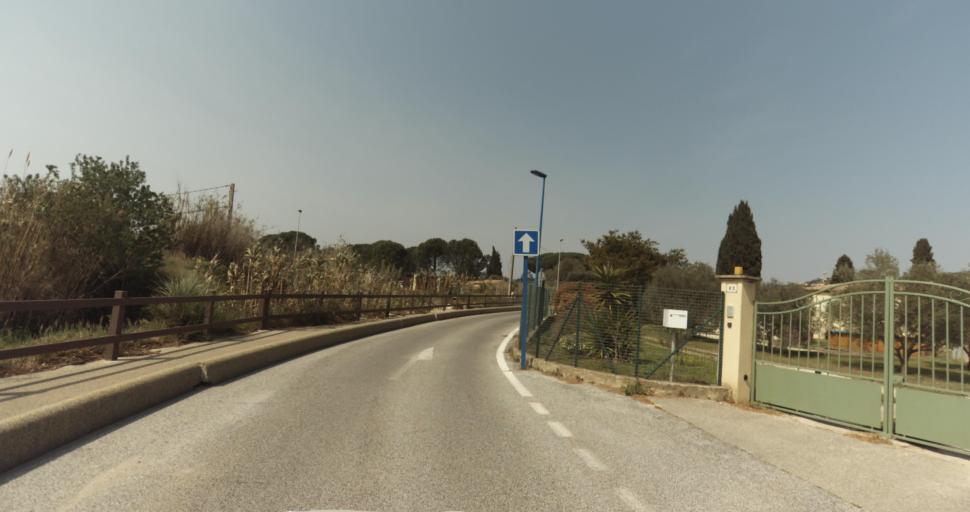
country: FR
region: Provence-Alpes-Cote d'Azur
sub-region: Departement du Var
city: Bormes-les-Mimosas
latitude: 43.1337
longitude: 6.3389
